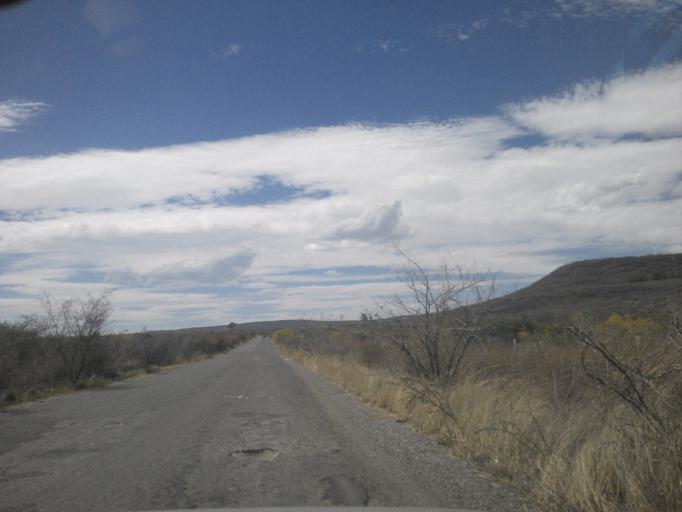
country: MX
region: Jalisco
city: San Diego de Alejandria
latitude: 20.8979
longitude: -101.9765
